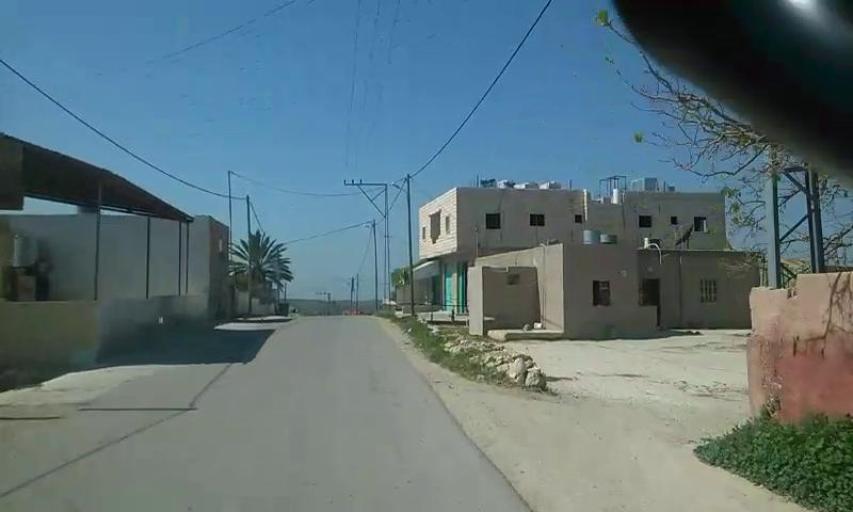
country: PS
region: West Bank
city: Al Majd
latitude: 31.4828
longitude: 34.9484
